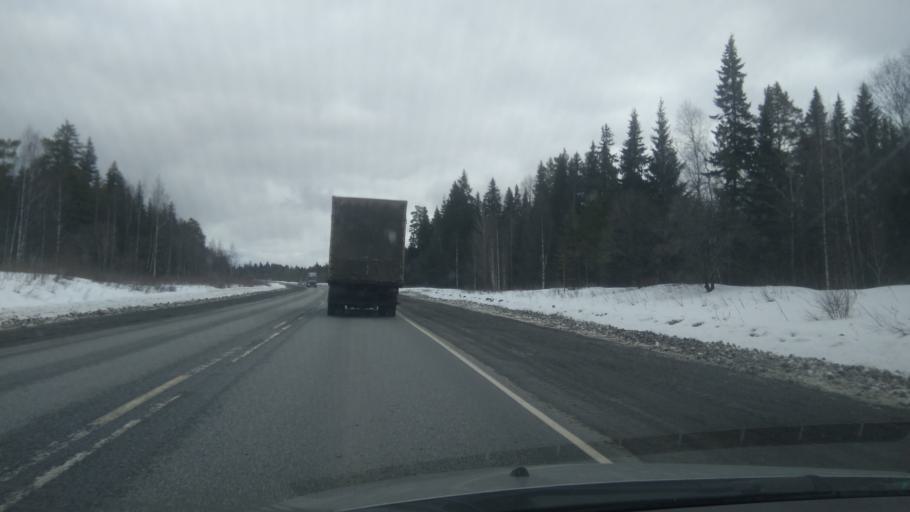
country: RU
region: Sverdlovsk
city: Atig
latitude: 56.7983
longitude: 59.3903
